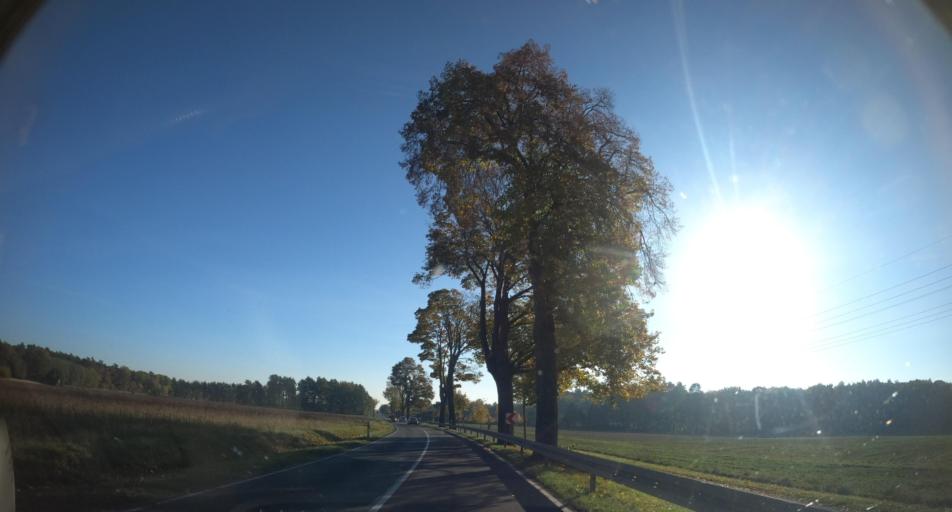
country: DE
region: Mecklenburg-Vorpommern
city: Ueckermunde
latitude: 53.7159
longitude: 14.0646
